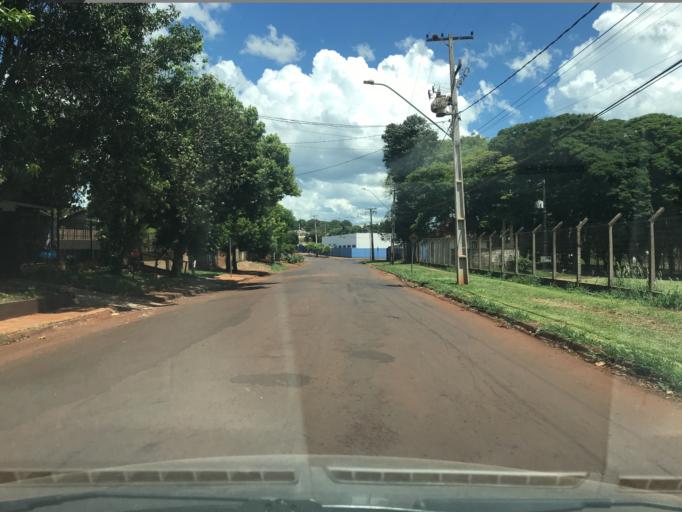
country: BR
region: Parana
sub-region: Palotina
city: Palotina
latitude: -24.2787
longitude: -53.8486
